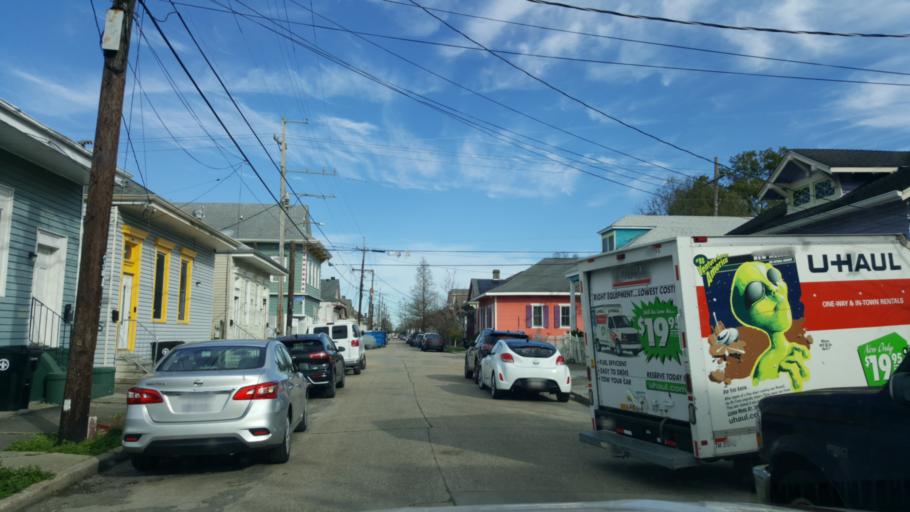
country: US
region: Louisiana
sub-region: Orleans Parish
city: New Orleans
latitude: 29.9702
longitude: -90.0545
